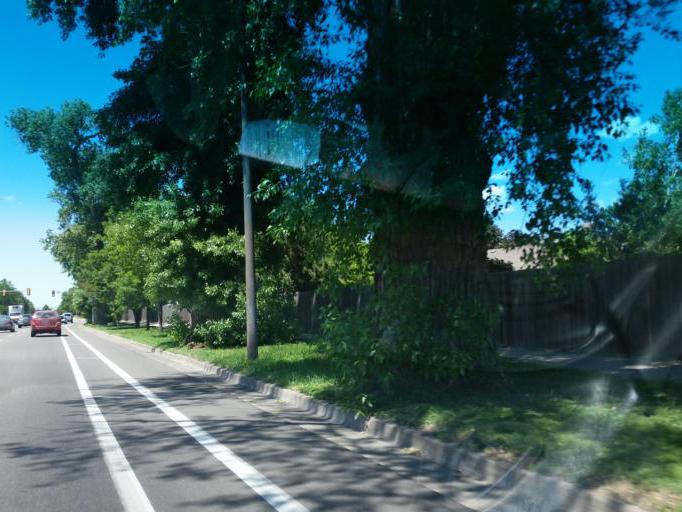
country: US
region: Colorado
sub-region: Larimer County
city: Fort Collins
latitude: 40.5477
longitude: -105.0961
